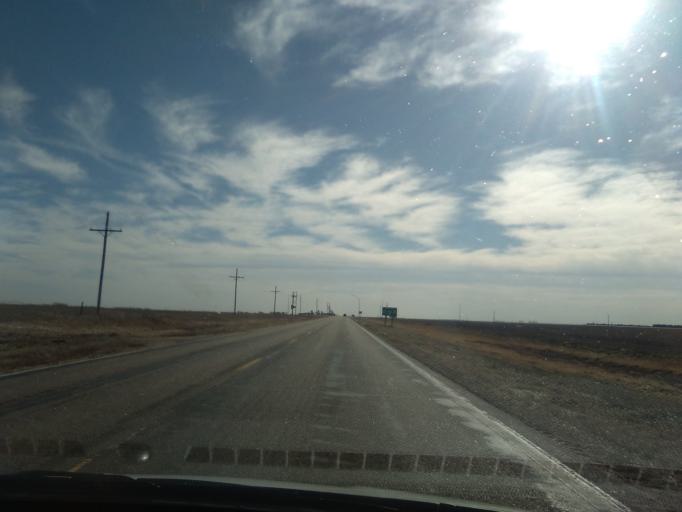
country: US
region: Nebraska
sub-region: Clay County
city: Harvard
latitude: 40.5865
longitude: -98.1091
